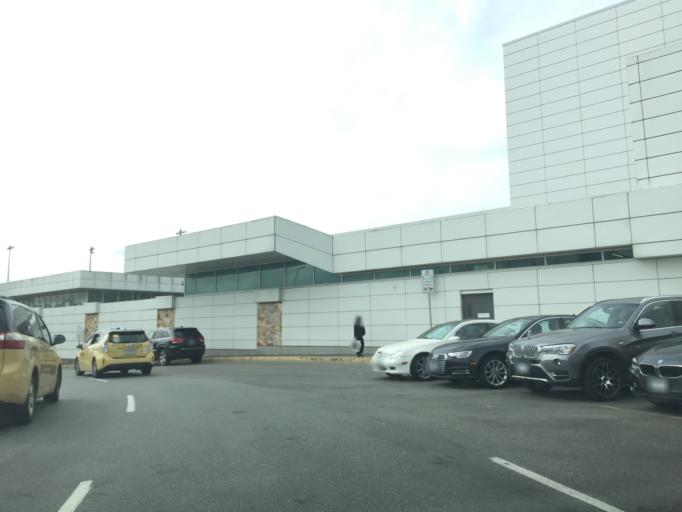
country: CA
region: British Columbia
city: Richmond
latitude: 49.1929
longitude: -123.1805
